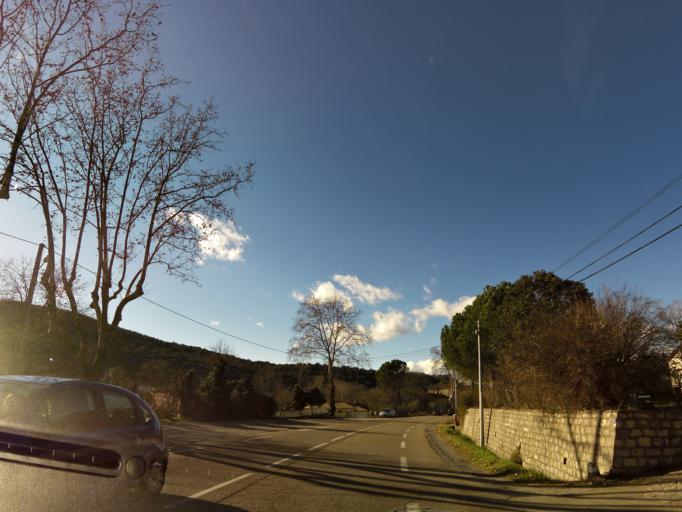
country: FR
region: Languedoc-Roussillon
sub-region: Departement du Gard
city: Sauve
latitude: 43.9366
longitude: 3.9608
